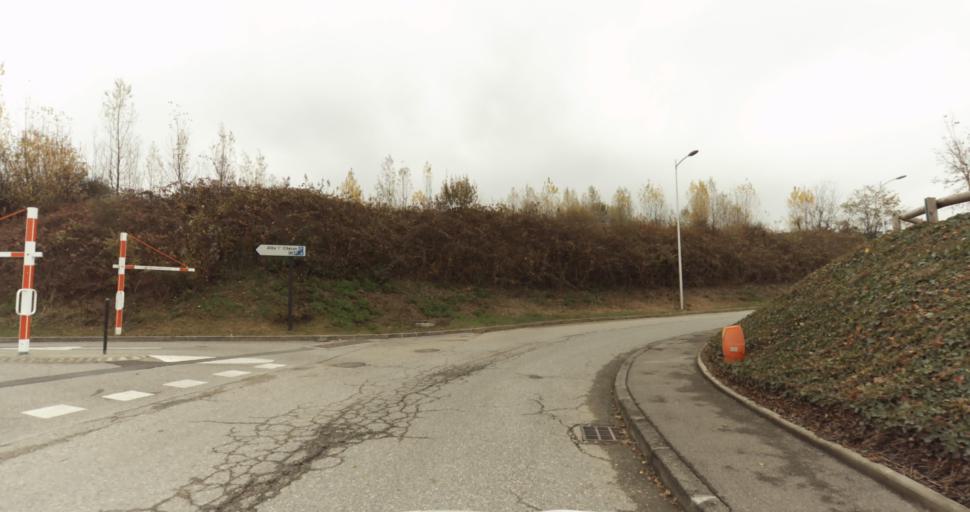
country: FR
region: Rhone-Alpes
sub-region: Departement de la Haute-Savoie
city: Alby-sur-Cheran
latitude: 45.8149
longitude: 6.0056
